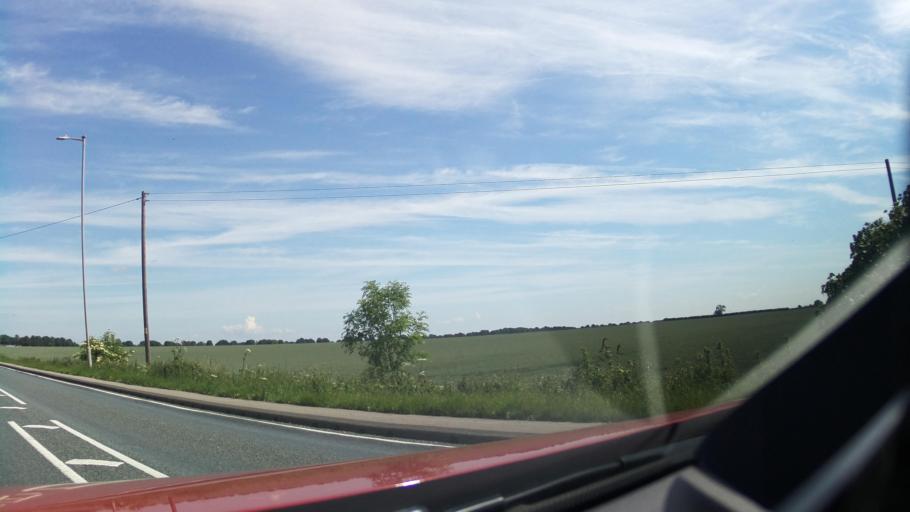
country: GB
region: England
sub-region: Lincolnshire
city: Burton
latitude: 53.2852
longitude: -0.5415
